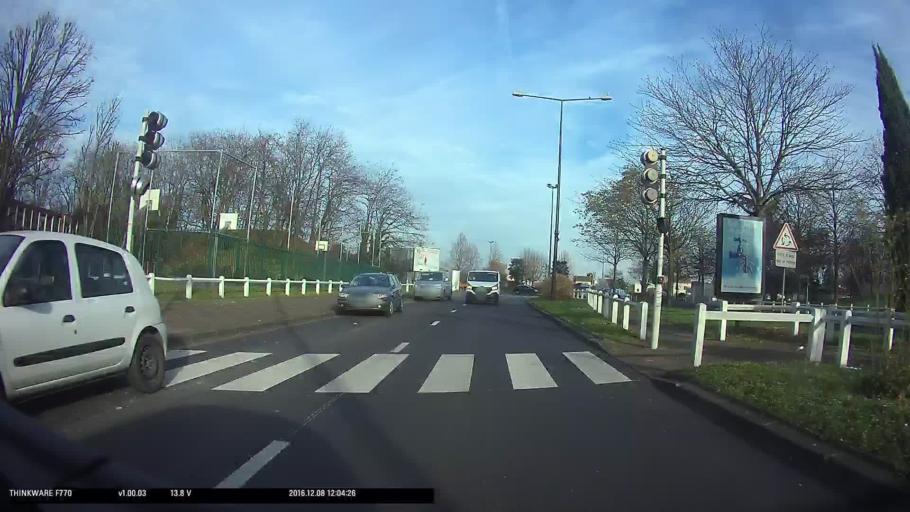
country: FR
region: Ile-de-France
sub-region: Departement de Seine-Saint-Denis
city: Bobigny
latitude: 48.9088
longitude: 2.4457
